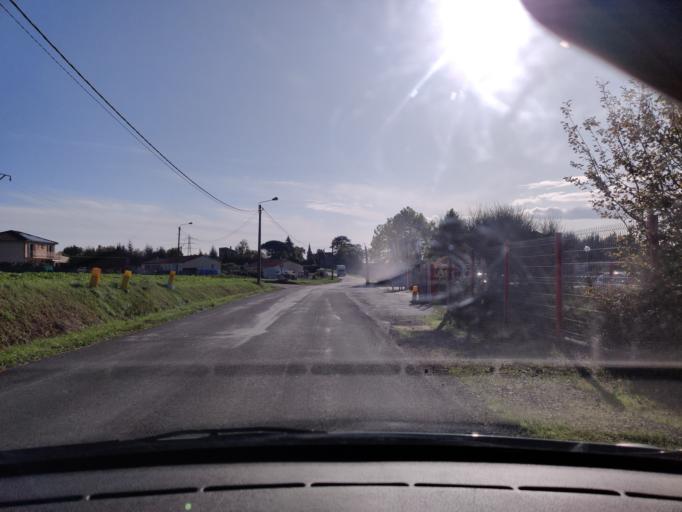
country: FR
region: Auvergne
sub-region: Departement du Puy-de-Dome
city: Aigueperse
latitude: 46.0264
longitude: 3.1929
